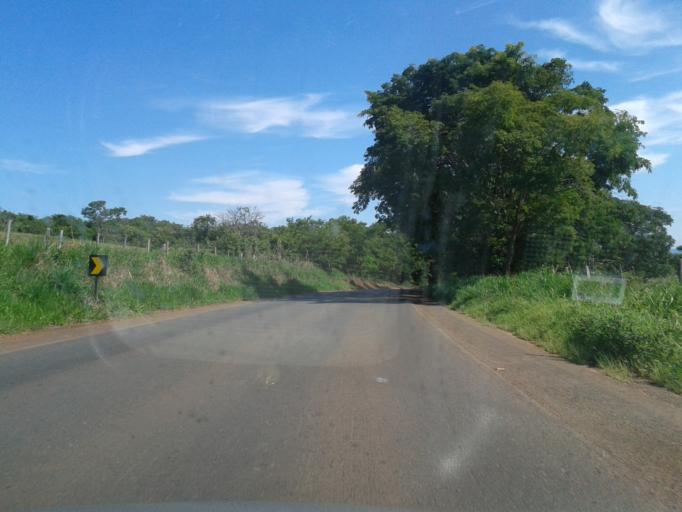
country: BR
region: Goias
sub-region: Piracanjuba
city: Piracanjuba
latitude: -17.2267
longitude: -48.7136
